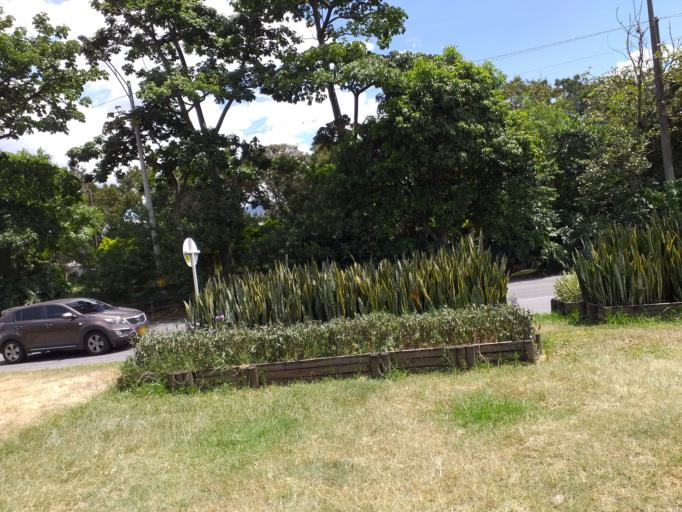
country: CO
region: Antioquia
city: Medellin
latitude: 6.2800
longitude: -75.5681
